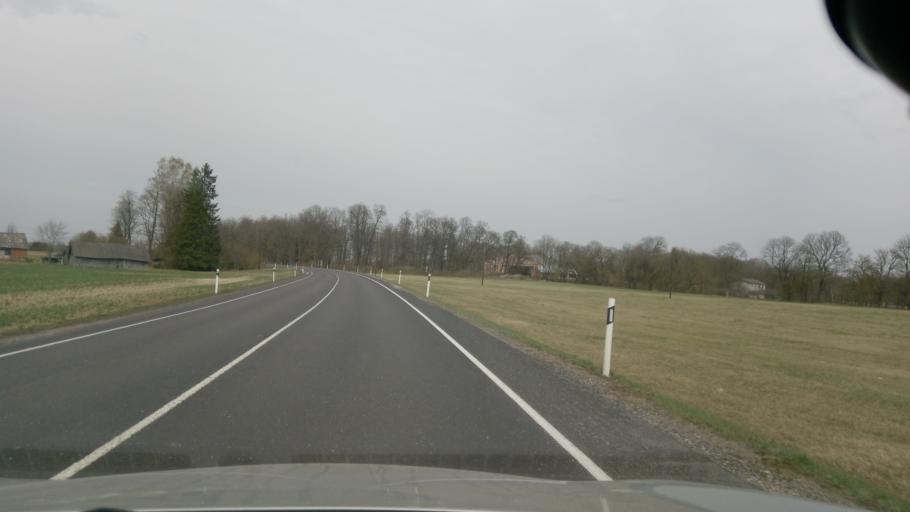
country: EE
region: Viljandimaa
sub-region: Vohma linn
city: Vohma
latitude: 58.6891
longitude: 25.6248
